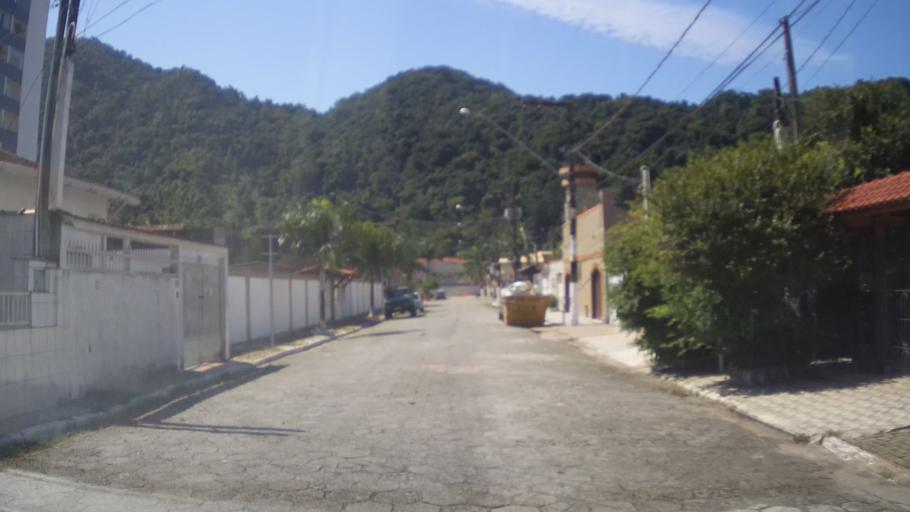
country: BR
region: Sao Paulo
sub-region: Praia Grande
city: Praia Grande
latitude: -24.0099
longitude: -46.3973
